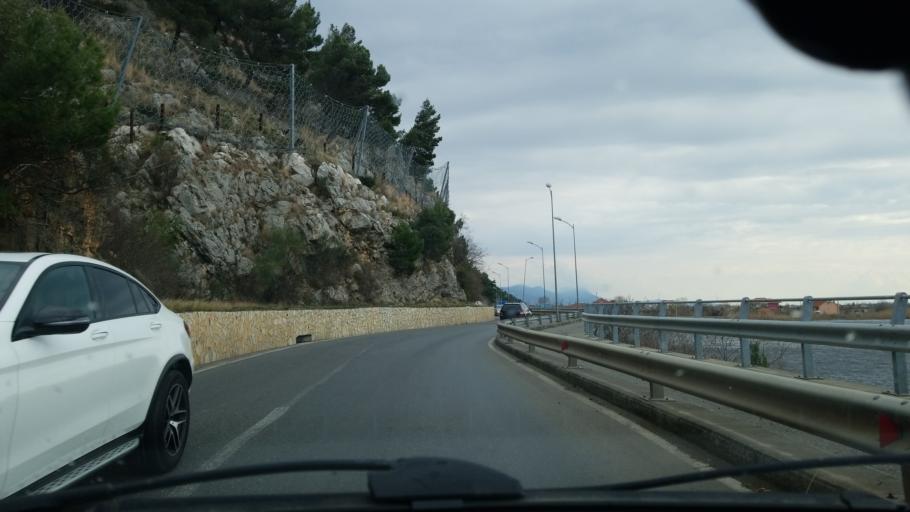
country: AL
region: Lezhe
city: Shengjin
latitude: 41.8035
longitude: 19.6143
